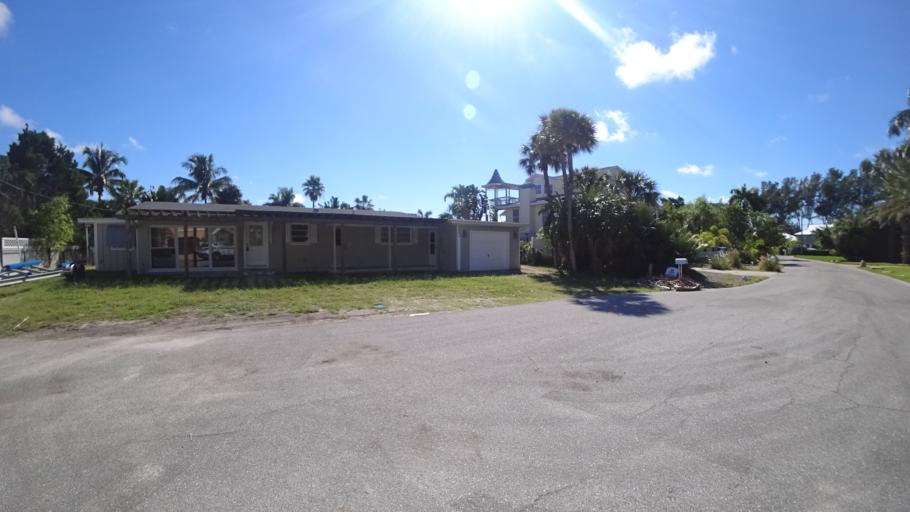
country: US
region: Florida
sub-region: Manatee County
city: Holmes Beach
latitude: 27.5113
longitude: -82.7118
